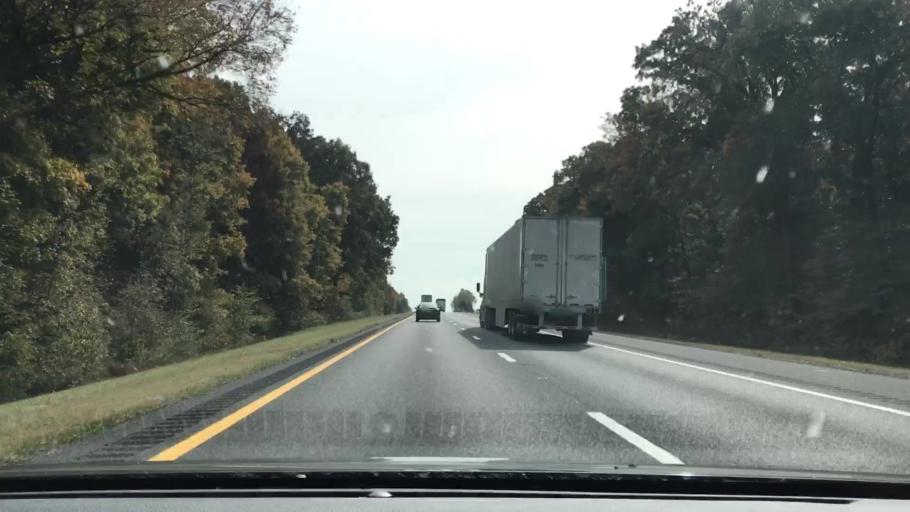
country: US
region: Tennessee
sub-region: Montgomery County
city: Clarksville
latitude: 36.5618
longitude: -87.2530
